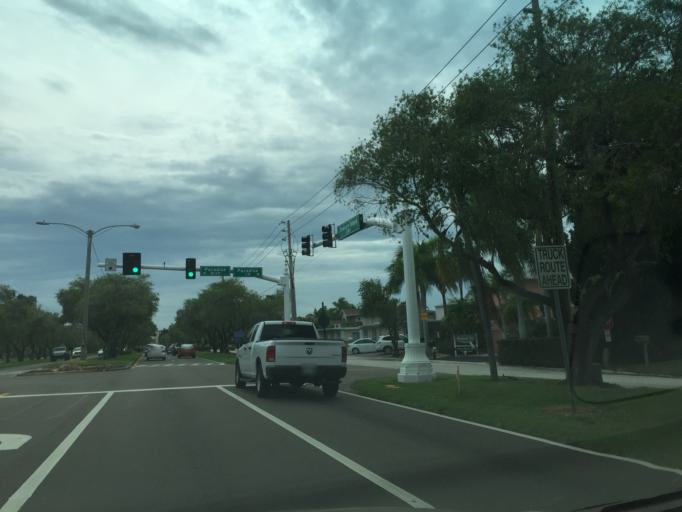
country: US
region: Florida
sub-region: Pinellas County
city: Treasure Island
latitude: 27.7708
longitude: -82.7585
